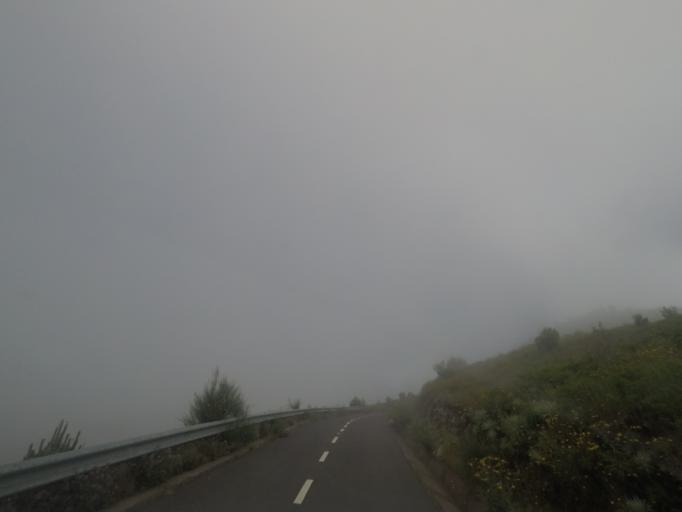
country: PT
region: Madeira
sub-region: Camara de Lobos
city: Curral das Freiras
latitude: 32.7045
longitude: -16.9403
